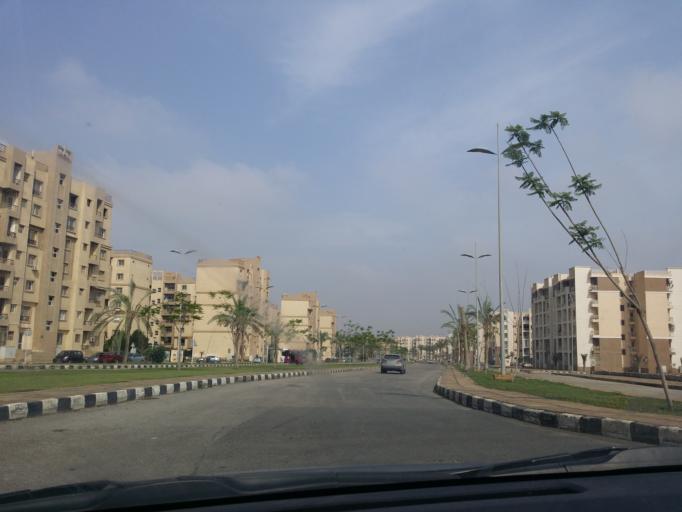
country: EG
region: Muhafazat al Qalyubiyah
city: Al Khankah
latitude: 30.0826
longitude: 31.6496
